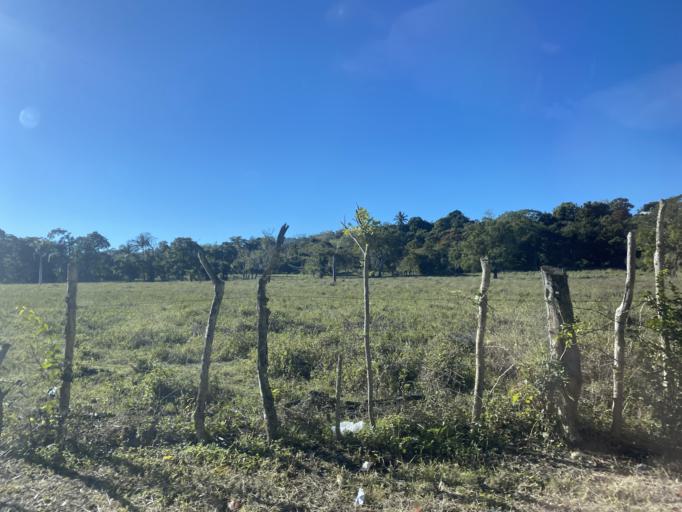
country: DO
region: Puerto Plata
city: Imbert
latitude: 19.7314
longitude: -70.8275
